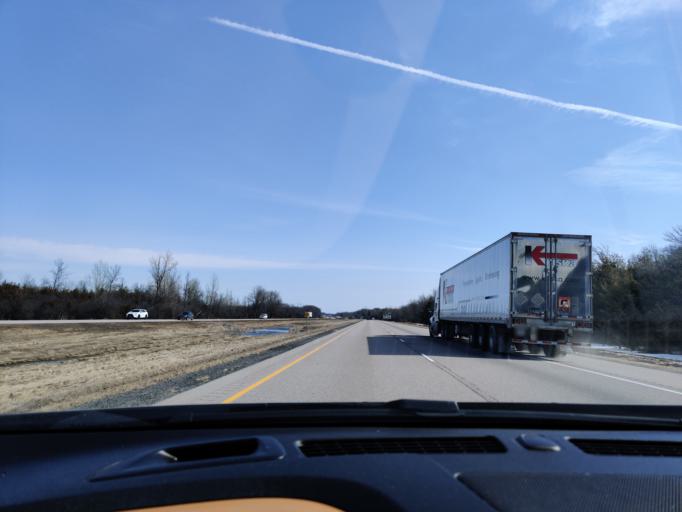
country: CA
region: Ontario
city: Skatepark
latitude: 44.2727
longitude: -76.9008
